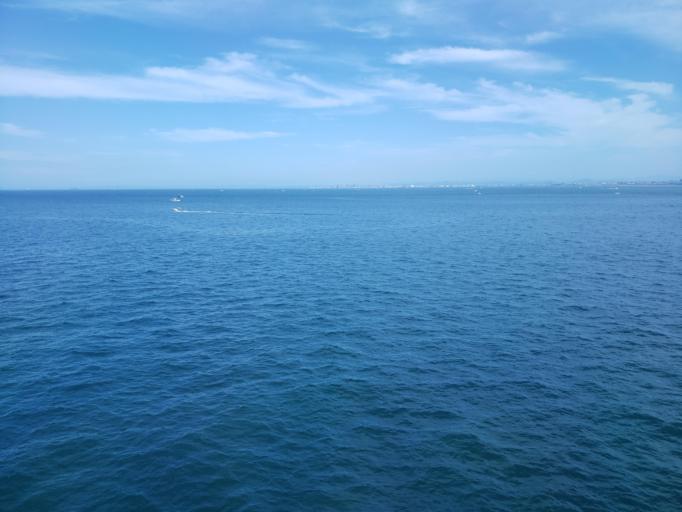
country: JP
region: Hyogo
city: Akashi
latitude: 34.6106
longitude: 134.9313
